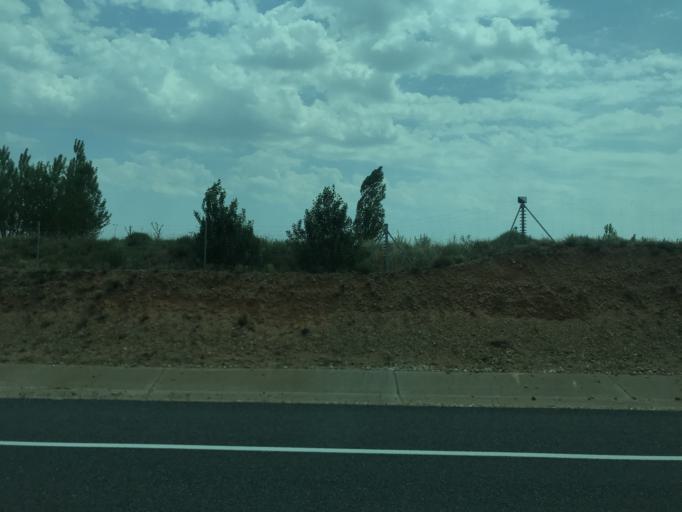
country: ES
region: Castille and Leon
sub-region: Provincia de Burgos
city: Madrigalejo del Monte
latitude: 42.1218
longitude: -3.7170
